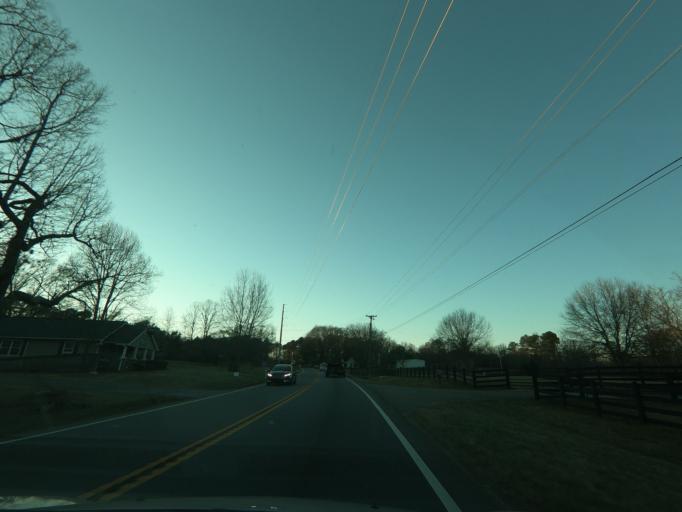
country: US
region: Georgia
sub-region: Forsyth County
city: Cumming
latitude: 34.2989
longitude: -84.1648
